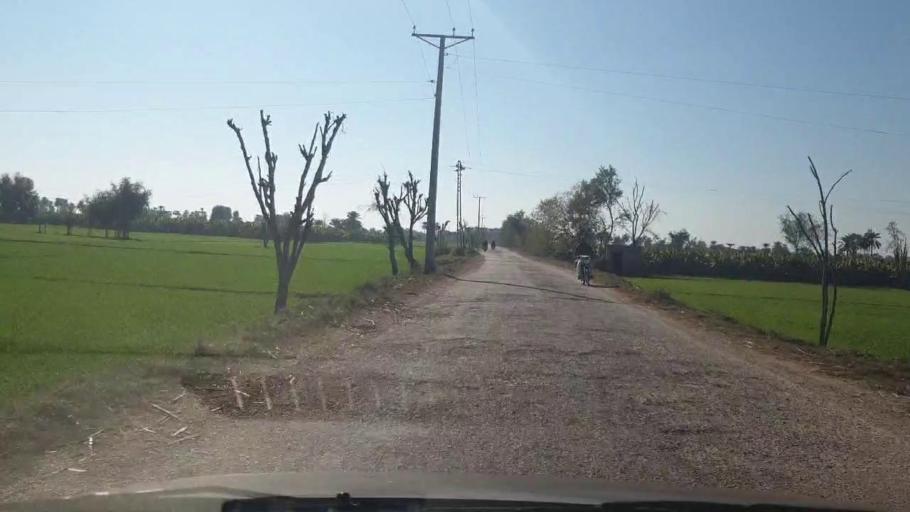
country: PK
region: Sindh
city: Bozdar
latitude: 27.2546
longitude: 68.6523
